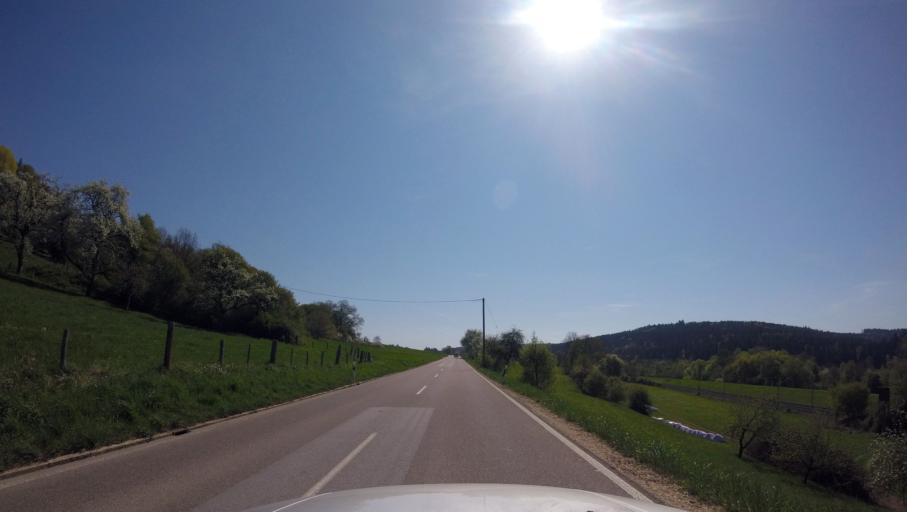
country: DE
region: Baden-Wuerttemberg
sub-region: Regierungsbezirk Stuttgart
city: Lorch
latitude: 48.7944
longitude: 9.7223
